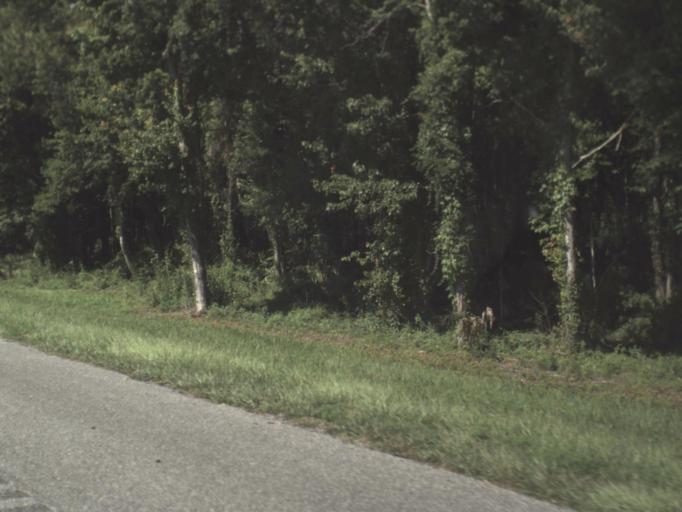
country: US
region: Florida
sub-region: Saint Johns County
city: Fruit Cove
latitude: 30.0479
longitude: -81.4972
